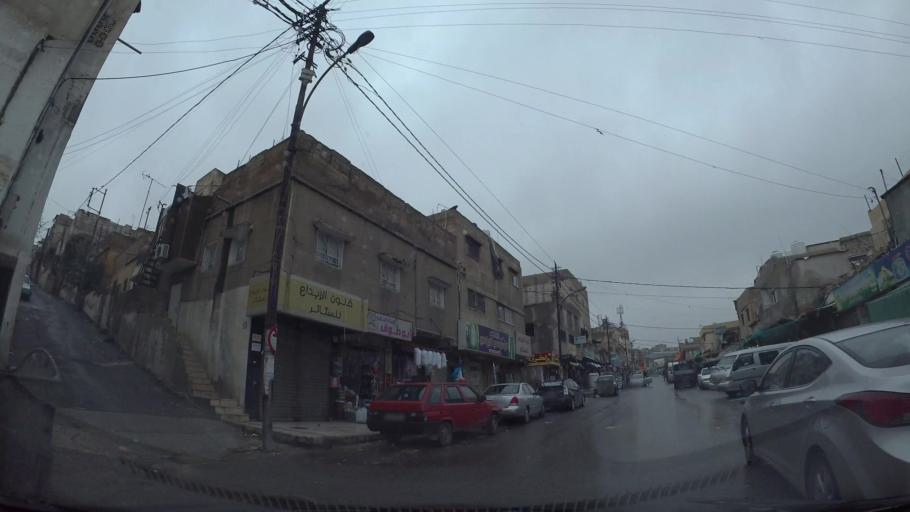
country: JO
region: Amman
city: Amman
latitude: 31.9649
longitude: 35.9261
